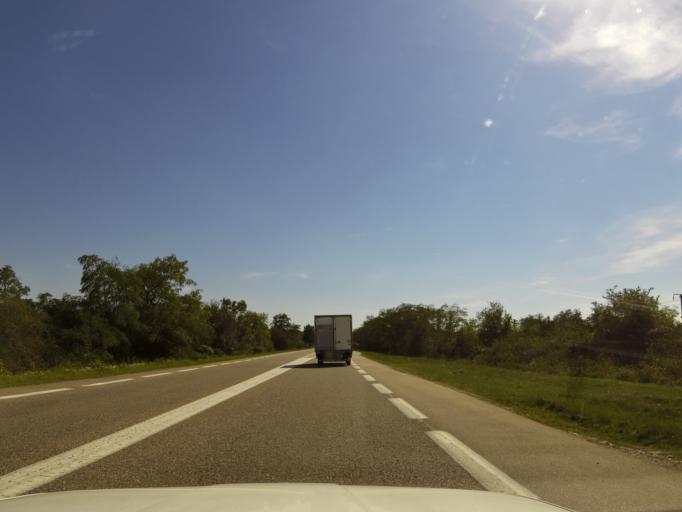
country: FR
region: Rhone-Alpes
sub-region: Departement du Rhone
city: Saint-Laurent-de-Mure
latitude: 45.6904
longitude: 5.0706
